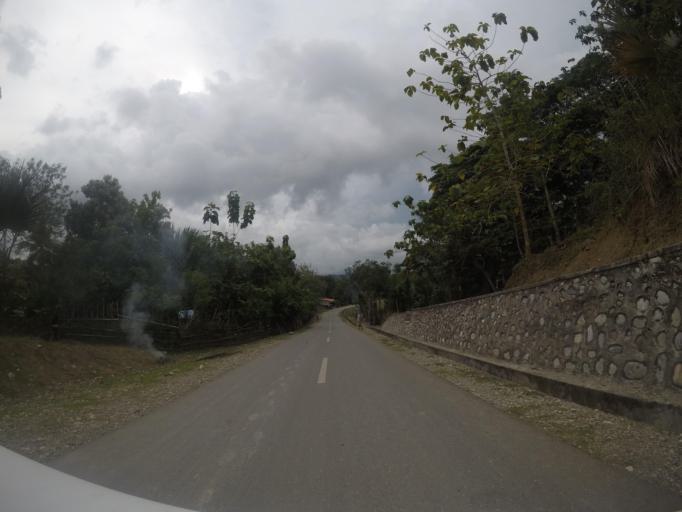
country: TL
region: Viqueque
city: Viqueque
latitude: -8.8657
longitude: 126.3692
